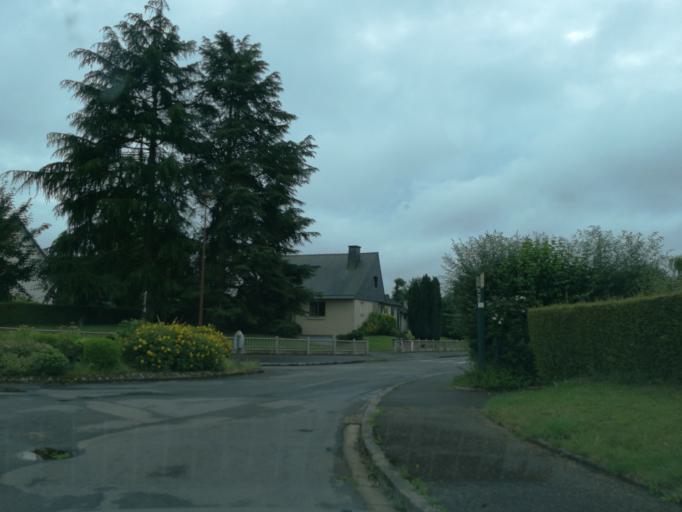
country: FR
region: Brittany
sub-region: Departement d'Ille-et-Vilaine
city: Bedee
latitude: 48.1768
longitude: -1.9429
